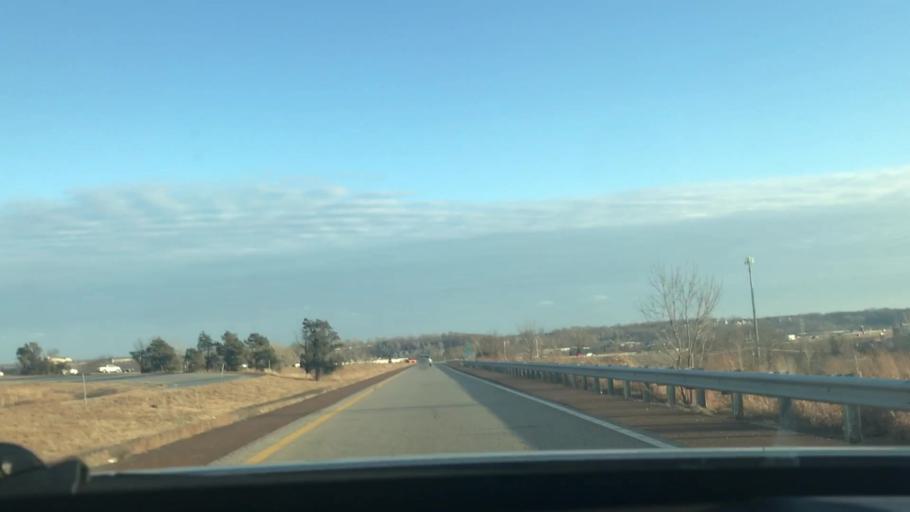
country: US
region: Missouri
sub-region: Jackson County
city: East Independence
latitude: 39.0402
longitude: -94.3651
